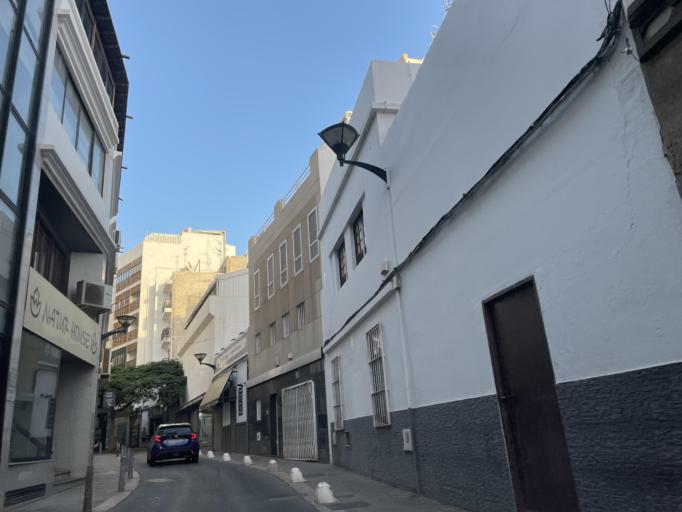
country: ES
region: Canary Islands
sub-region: Provincia de Las Palmas
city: Arrecife
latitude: 28.9590
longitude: -13.5493
